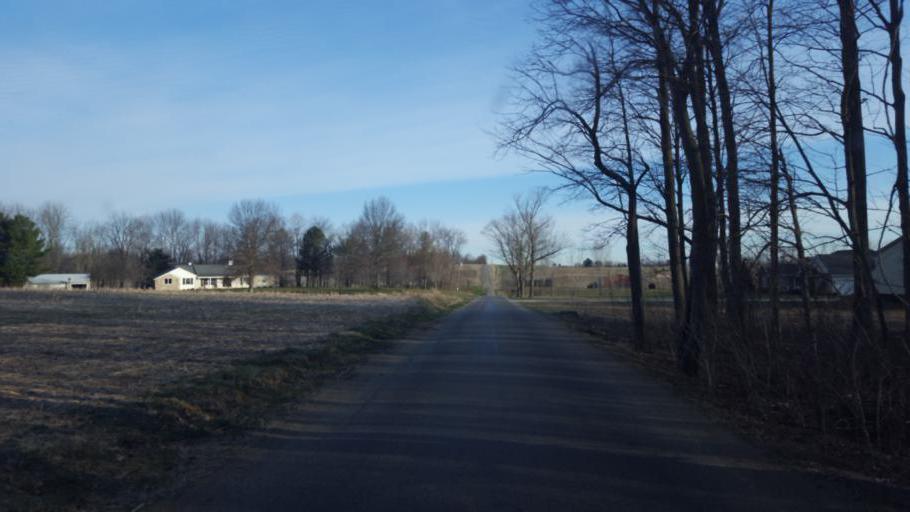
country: US
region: Ohio
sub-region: Knox County
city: Fredericktown
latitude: 40.4882
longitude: -82.5762
